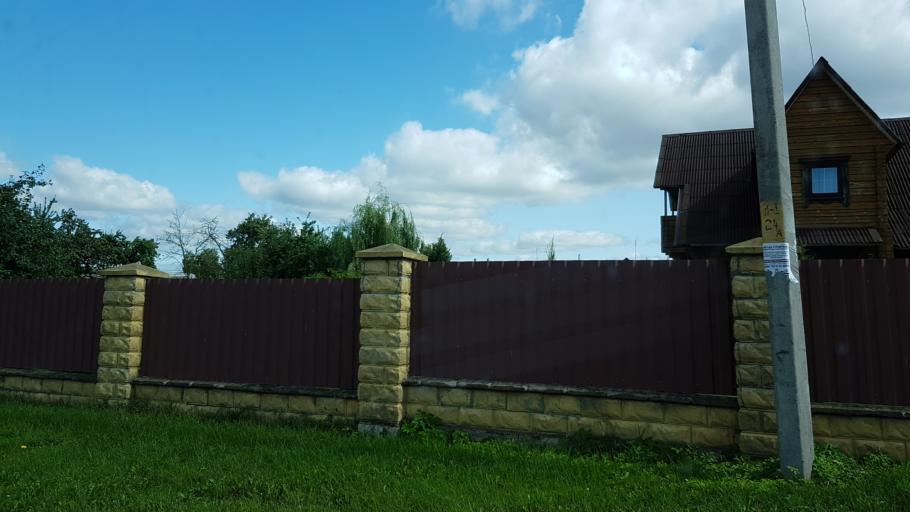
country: BY
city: Fanipol
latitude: 53.7614
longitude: 27.3328
